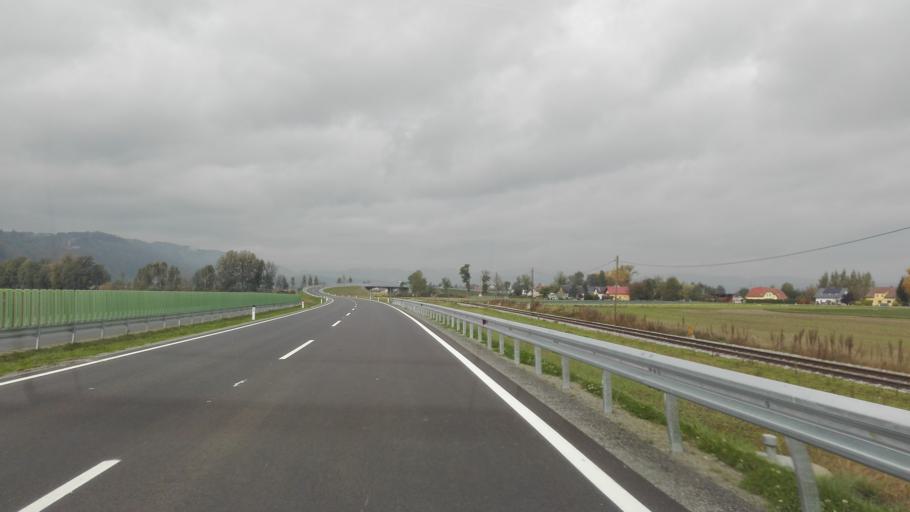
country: AT
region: Upper Austria
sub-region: Politischer Bezirk Urfahr-Umgebung
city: Feldkirchen an der Donau
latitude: 48.3260
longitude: 14.0089
